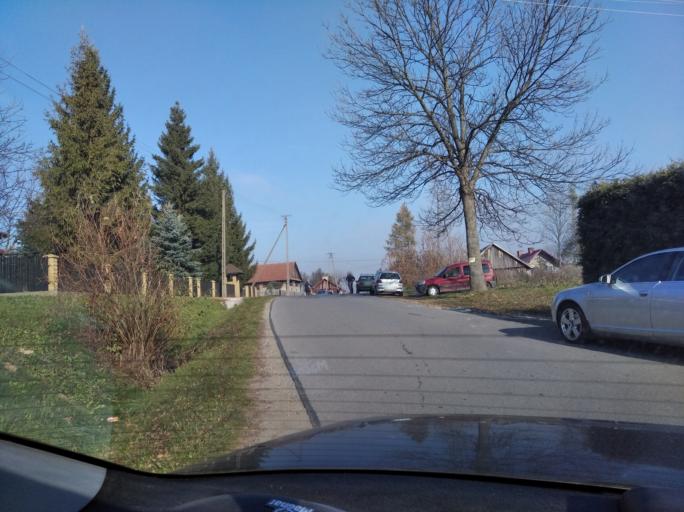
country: PL
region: Subcarpathian Voivodeship
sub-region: Powiat strzyzowski
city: Wysoka Strzyzowska
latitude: 49.8330
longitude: 21.7410
